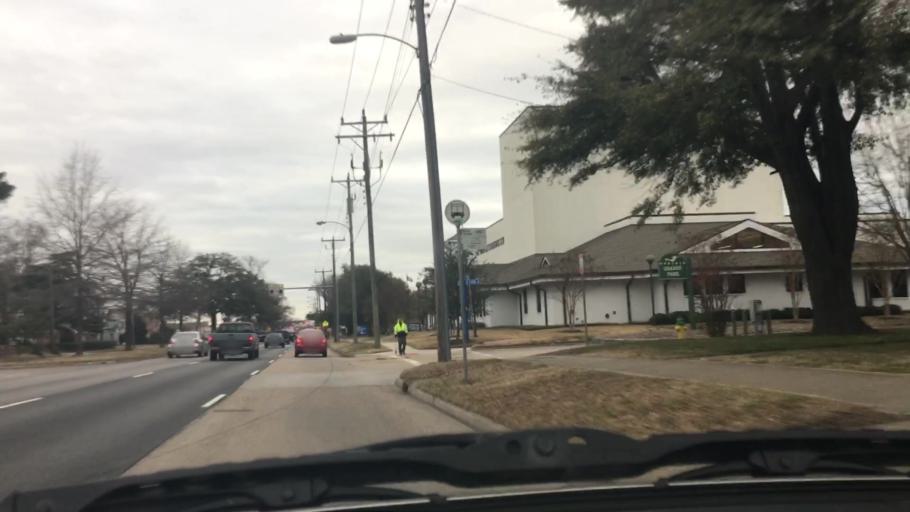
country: US
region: Virginia
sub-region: City of Norfolk
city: Norfolk
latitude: 36.9099
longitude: -76.2746
